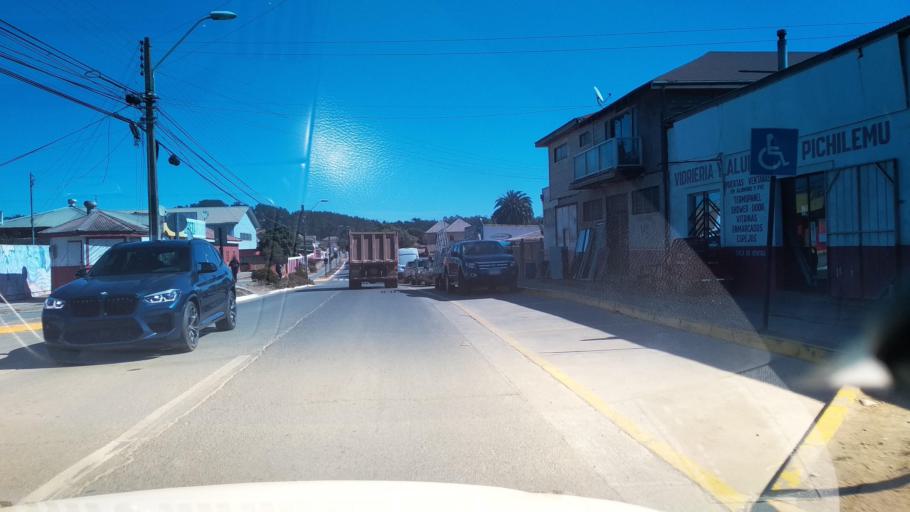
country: CL
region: O'Higgins
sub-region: Provincia de Colchagua
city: Santa Cruz
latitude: -34.3898
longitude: -72.0025
